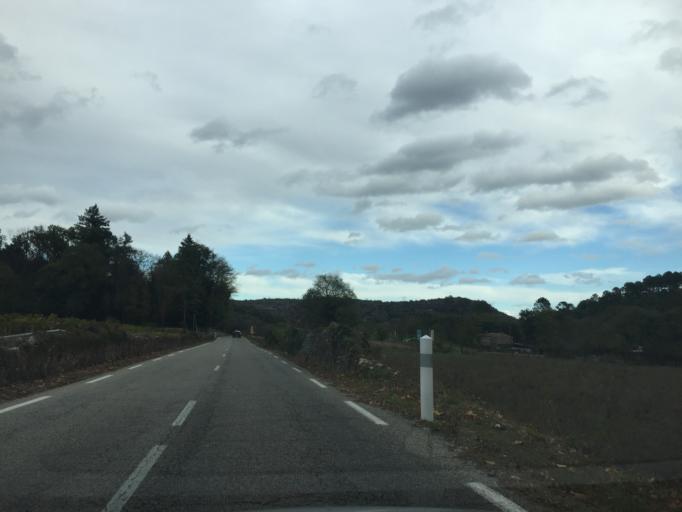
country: FR
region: Rhone-Alpes
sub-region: Departement de l'Ardeche
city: Les Vans
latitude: 44.4152
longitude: 4.1599
